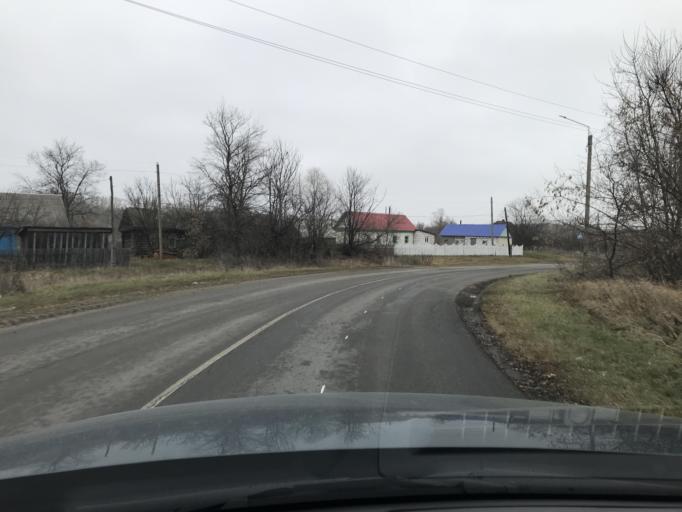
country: RU
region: Penza
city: Zemetchino
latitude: 53.6126
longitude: 42.6780
